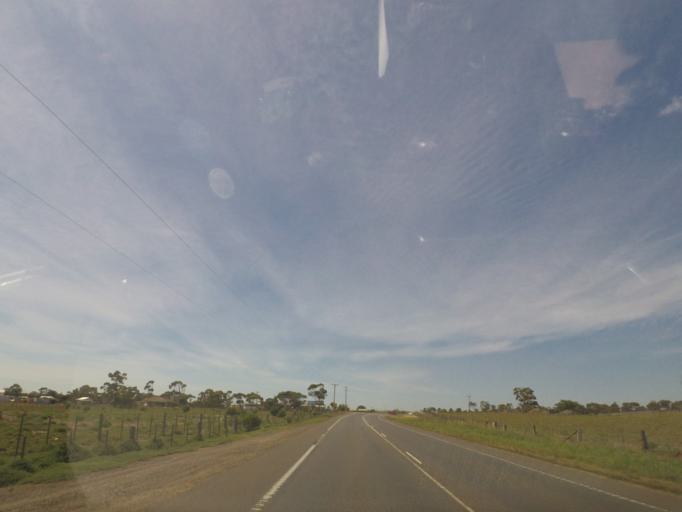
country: AU
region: Victoria
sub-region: Moorabool
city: Bacchus Marsh
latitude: -37.7039
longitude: 144.4570
